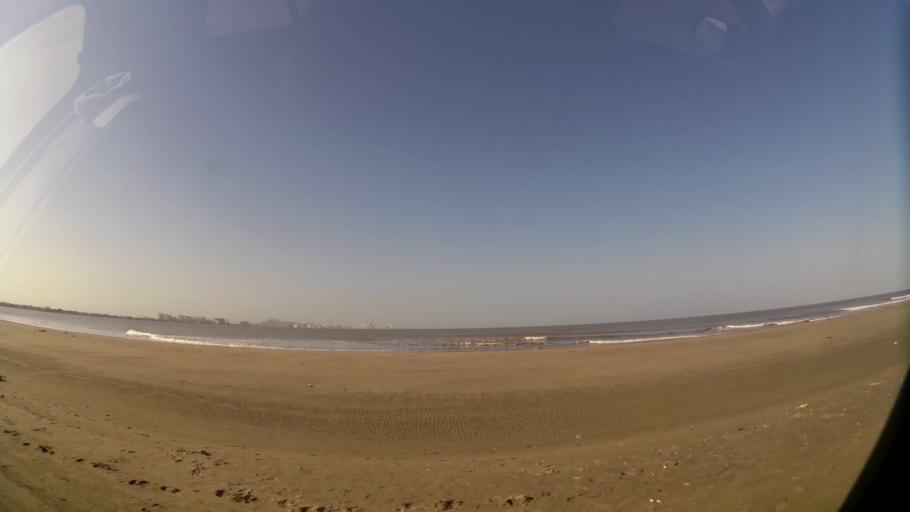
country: CO
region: Bolivar
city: Cartagena
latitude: 10.4934
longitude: -75.4960
